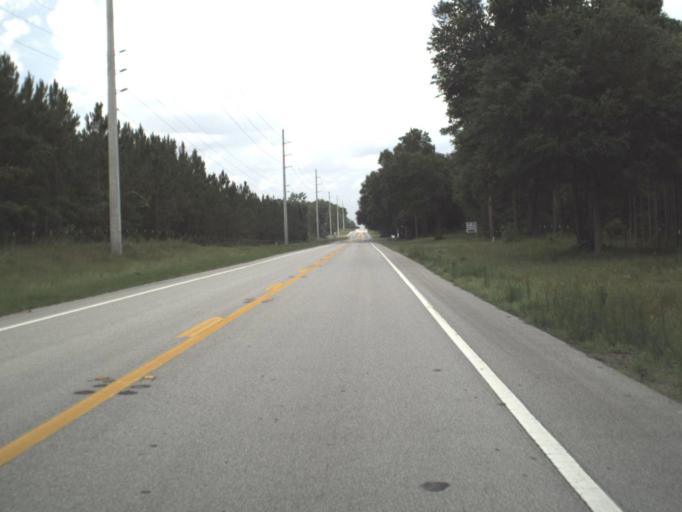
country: US
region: Florida
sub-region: Madison County
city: Madison
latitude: 30.4749
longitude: -83.2611
